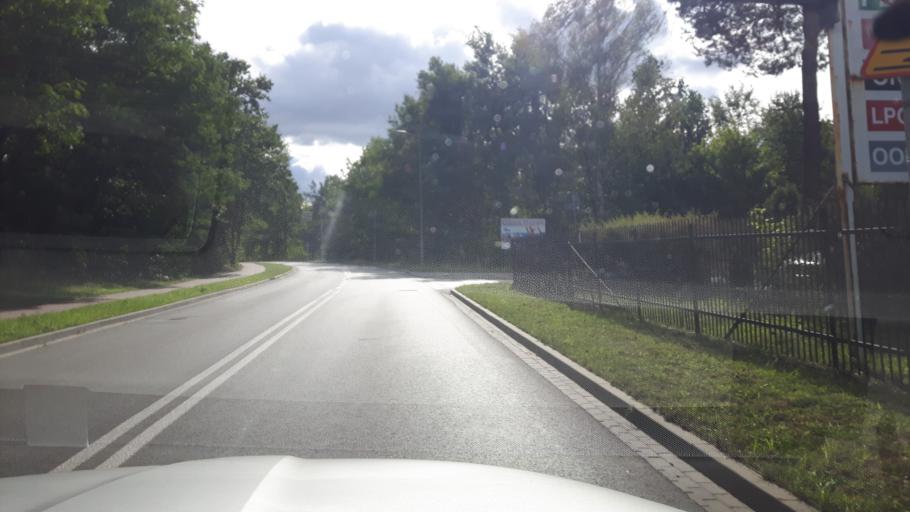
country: PL
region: Masovian Voivodeship
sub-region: Powiat wolominski
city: Wolomin
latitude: 52.3633
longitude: 21.2246
